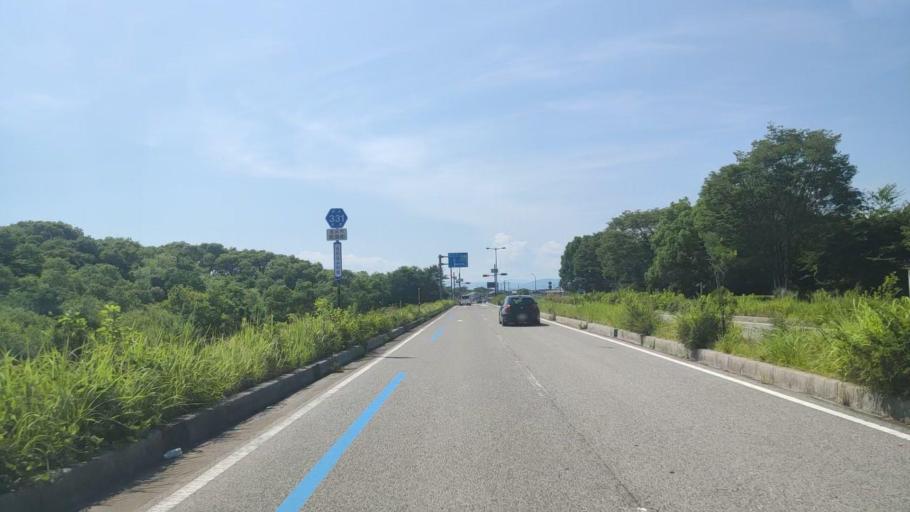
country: JP
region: Shiga Prefecture
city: Nagahama
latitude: 35.3848
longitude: 136.2482
